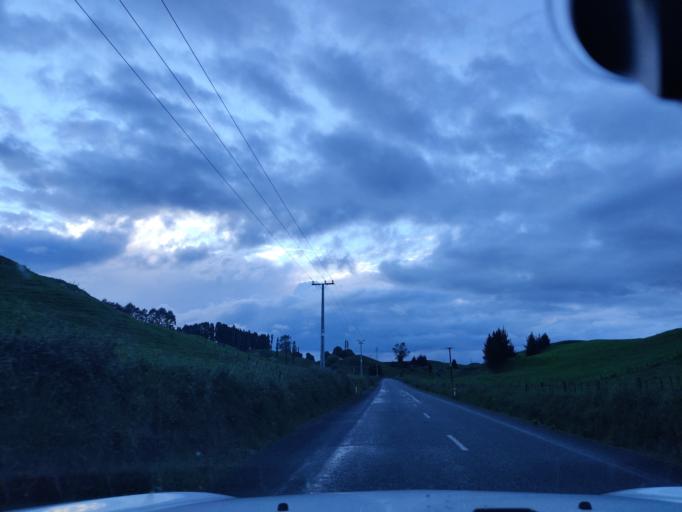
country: NZ
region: Waikato
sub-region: South Waikato District
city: Tokoroa
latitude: -38.1985
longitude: 175.8077
